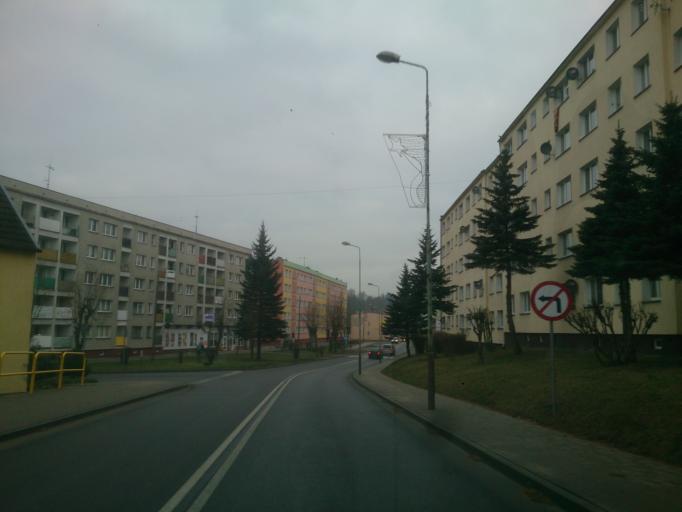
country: PL
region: Pomeranian Voivodeship
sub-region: Powiat bytowski
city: Miastko
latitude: 54.0054
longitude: 16.9820
